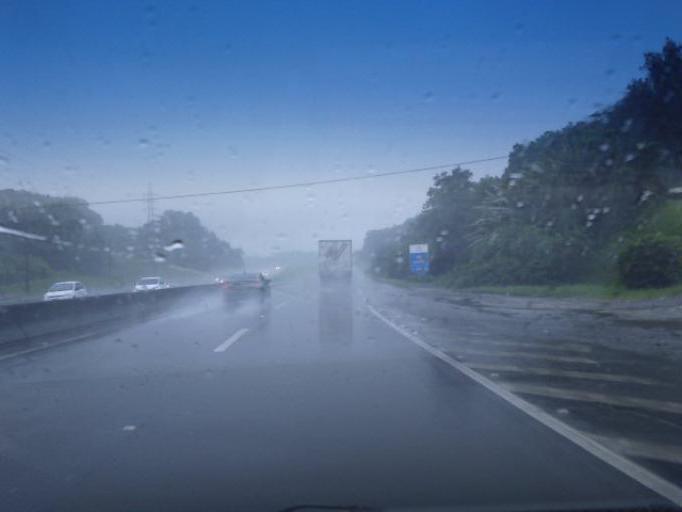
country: BR
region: Santa Catarina
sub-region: Joinville
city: Joinville
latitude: -26.3715
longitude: -48.8567
